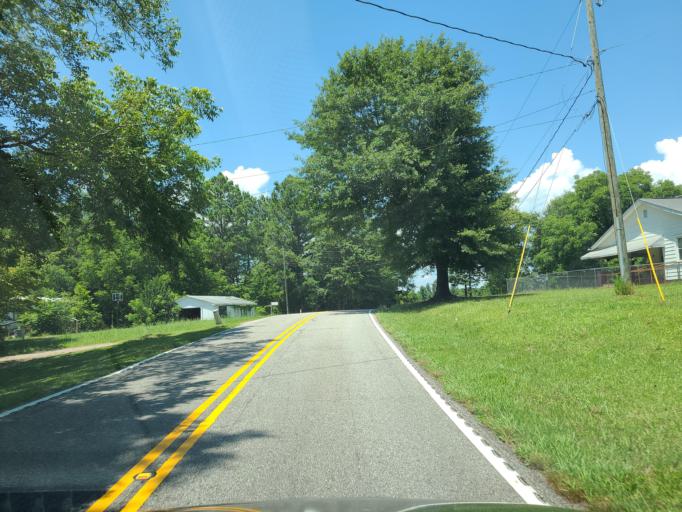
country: US
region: South Carolina
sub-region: Spartanburg County
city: Duncan
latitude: 34.9724
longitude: -82.1759
